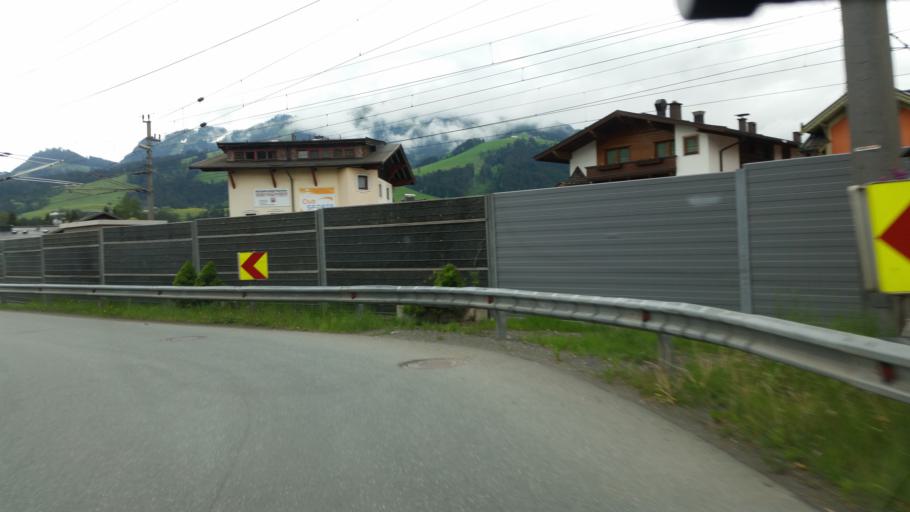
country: AT
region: Tyrol
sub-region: Politischer Bezirk Kitzbuhel
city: Kirchberg in Tirol
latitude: 47.4490
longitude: 12.3121
